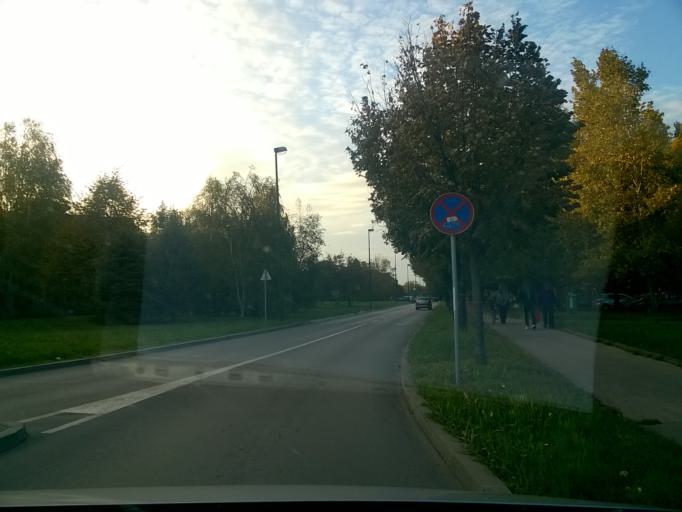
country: RS
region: Autonomna Pokrajina Vojvodina
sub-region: Juznobanatski Okrug
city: Pancevo
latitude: 44.8804
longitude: 20.6480
